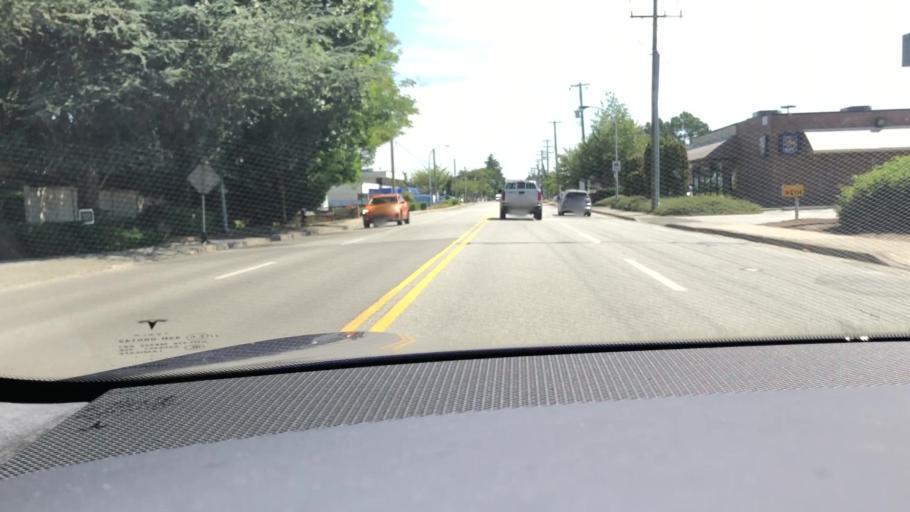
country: CA
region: British Columbia
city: Richmond
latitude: 49.1845
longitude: -123.0949
